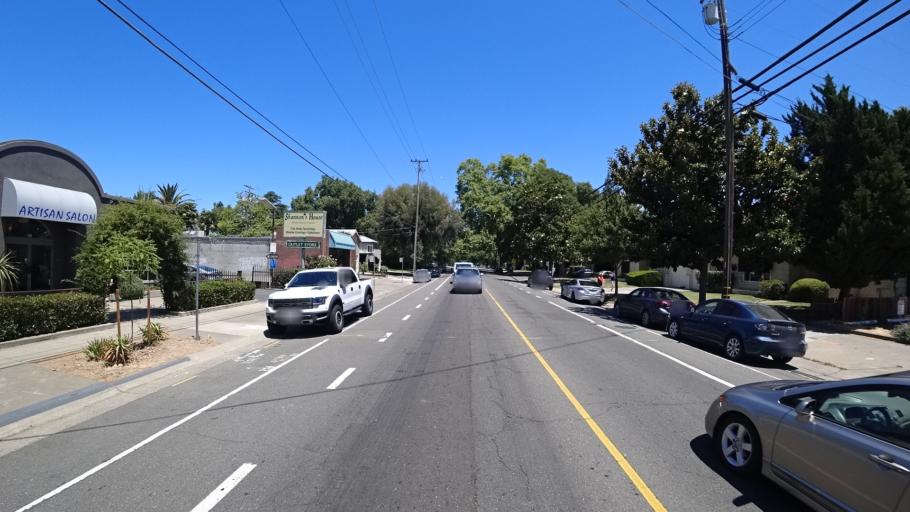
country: US
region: California
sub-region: Sacramento County
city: Sacramento
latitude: 38.5505
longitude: -121.5057
